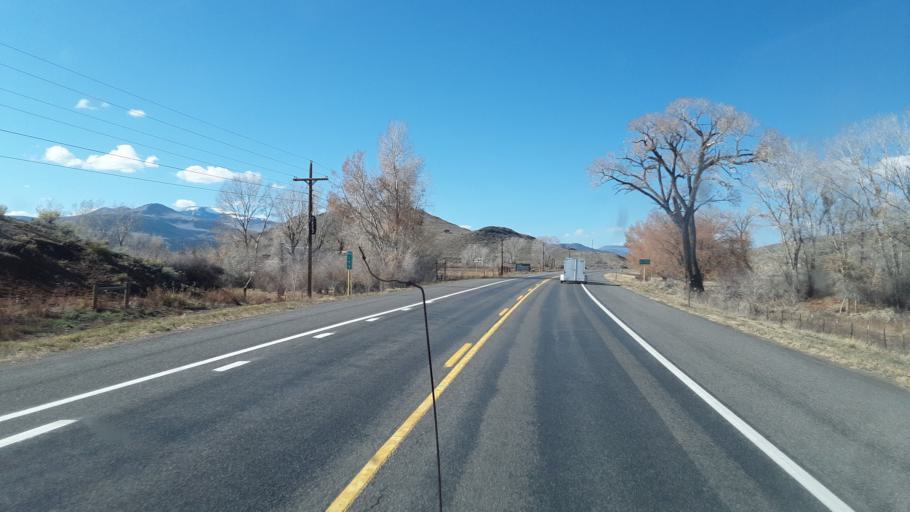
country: US
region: Colorado
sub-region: Rio Grande County
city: Del Norte
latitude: 37.6732
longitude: -106.4076
